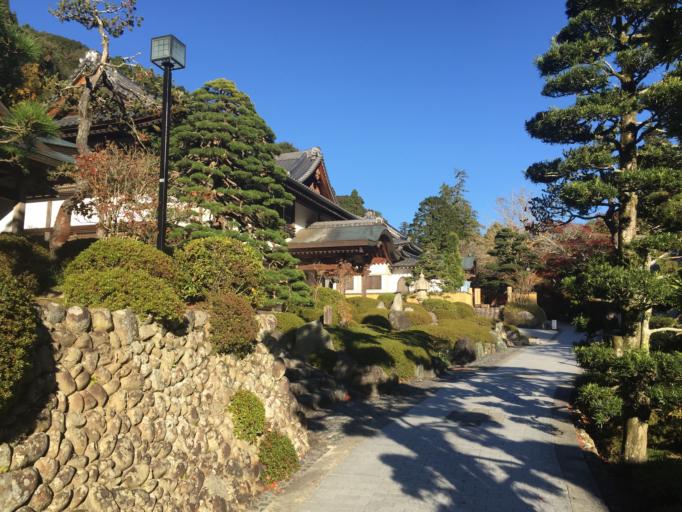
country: JP
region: Shizuoka
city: Kakegawa
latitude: 34.7352
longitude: 137.9743
